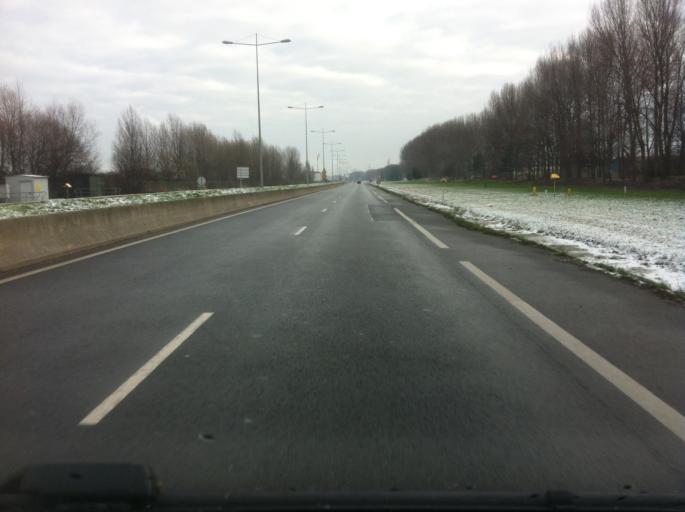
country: FR
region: Haute-Normandie
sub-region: Departement de la Seine-Maritime
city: Harfleur
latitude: 49.4869
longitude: 0.2169
